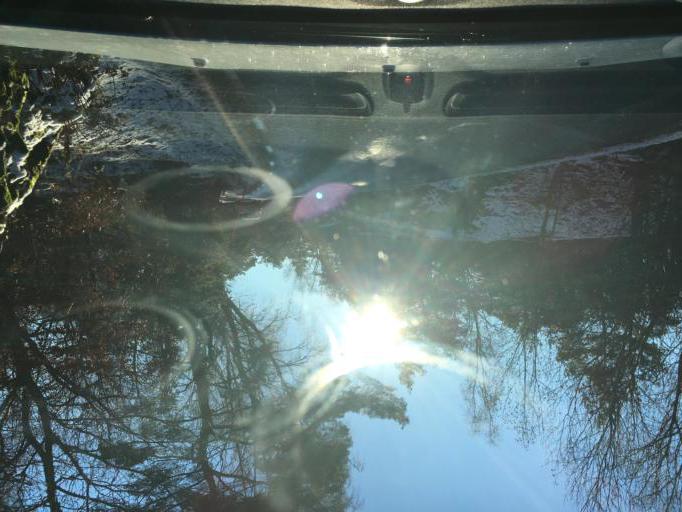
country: SE
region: Vaestra Goetaland
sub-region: Tjorns Kommun
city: Myggenas
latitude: 58.0619
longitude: 11.6822
